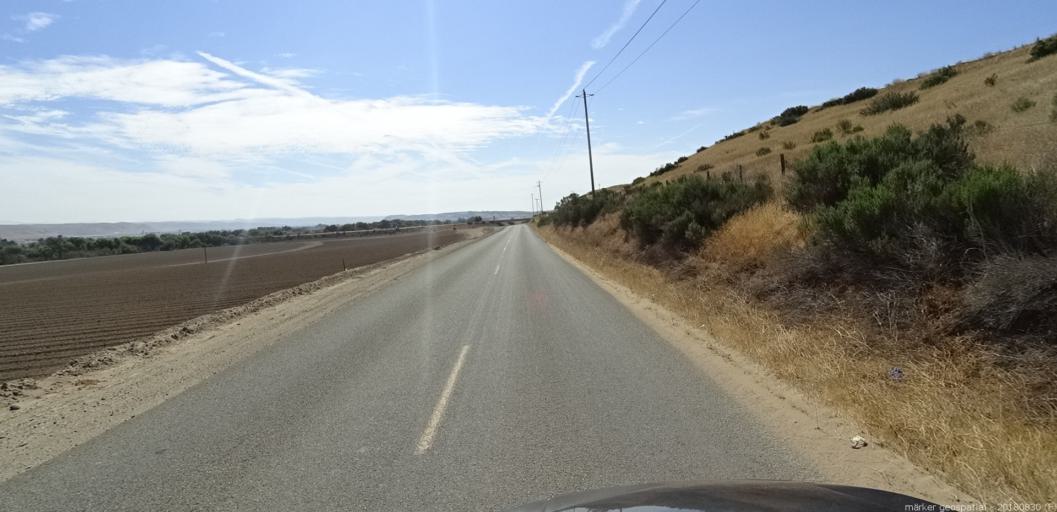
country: US
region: California
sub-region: Monterey County
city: King City
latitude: 36.1070
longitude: -121.0290
